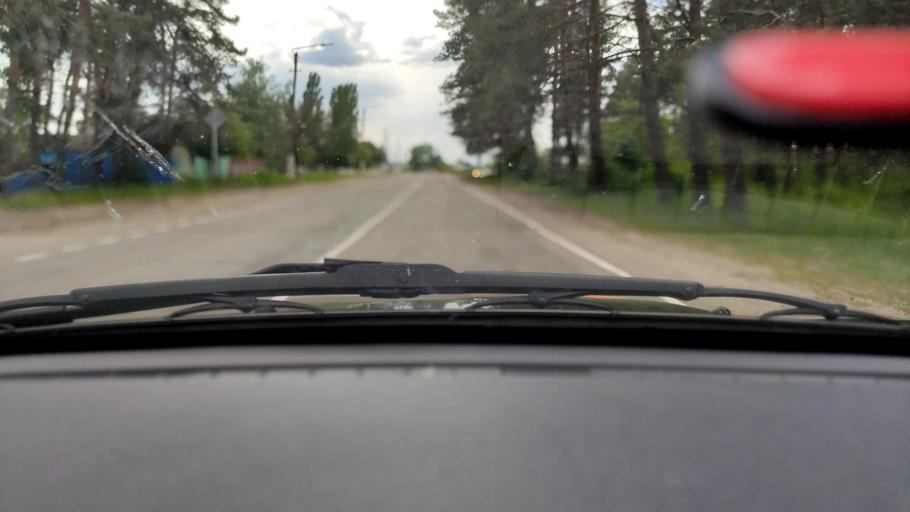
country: RU
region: Voronezj
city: Rossosh'
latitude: 51.0881
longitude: 38.6487
